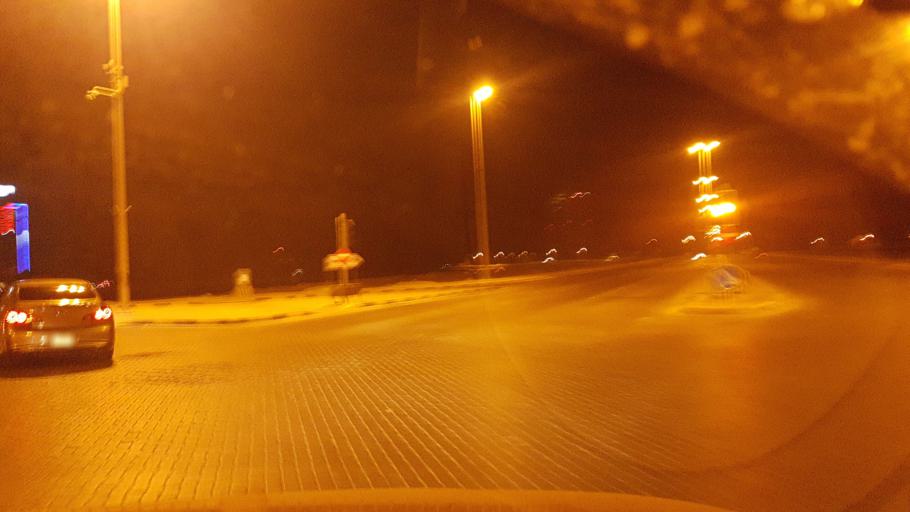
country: BH
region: Manama
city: Jidd Hafs
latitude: 26.2350
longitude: 50.5605
